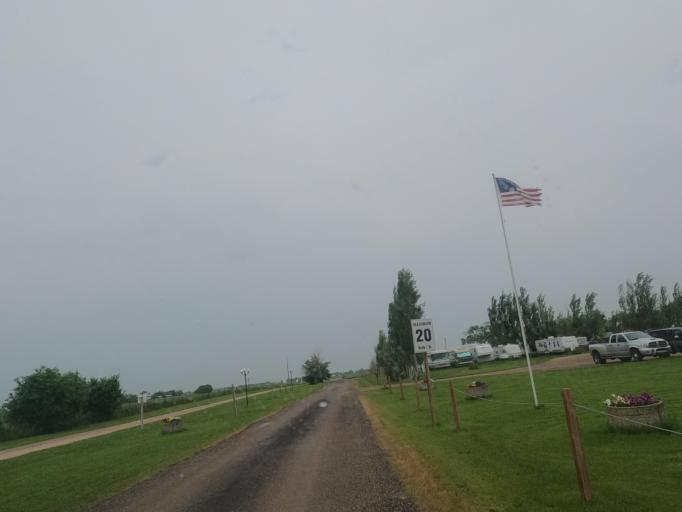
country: CA
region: Manitoba
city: Winnipeg
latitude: 49.8268
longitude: -96.9787
